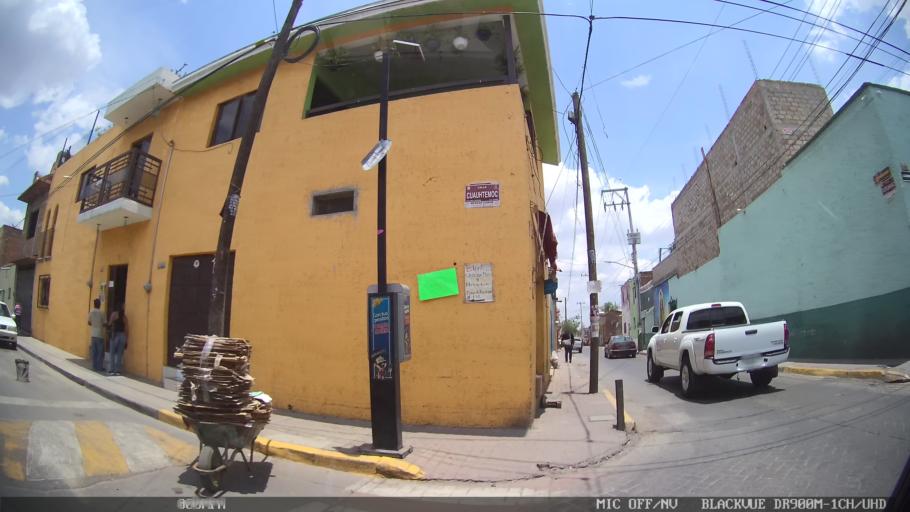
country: MX
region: Jalisco
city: Tonala
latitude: 20.6242
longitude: -103.2383
